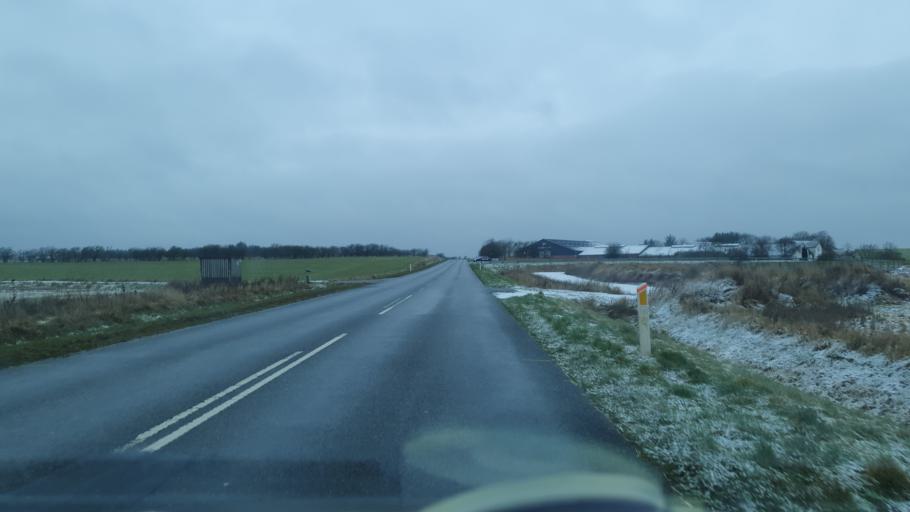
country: DK
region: North Denmark
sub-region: Jammerbugt Kommune
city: Brovst
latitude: 57.1214
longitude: 9.4934
